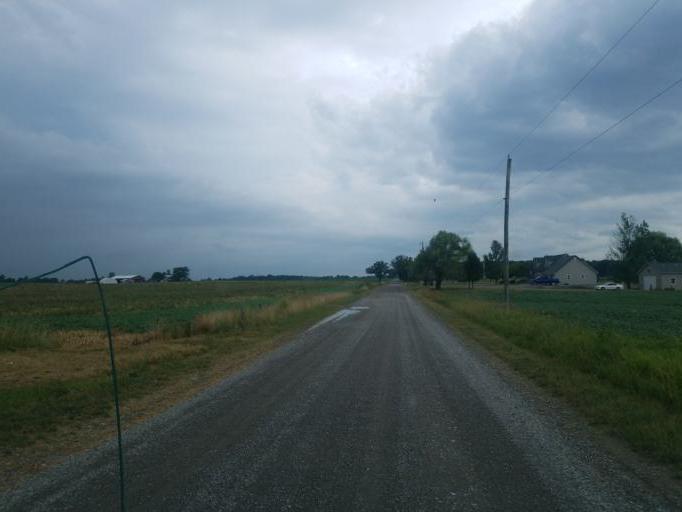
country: US
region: Ohio
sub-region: Defiance County
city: Hicksville
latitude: 41.3218
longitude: -84.8040
